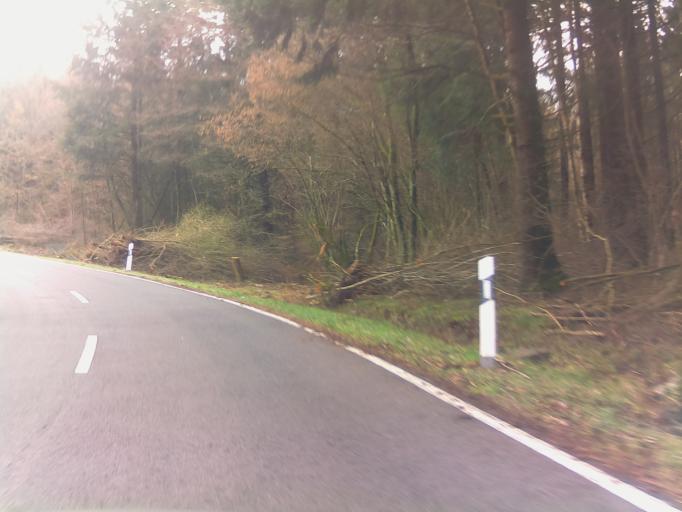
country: DE
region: Rheinland-Pfalz
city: Oberhambach
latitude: 49.6815
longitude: 7.1568
